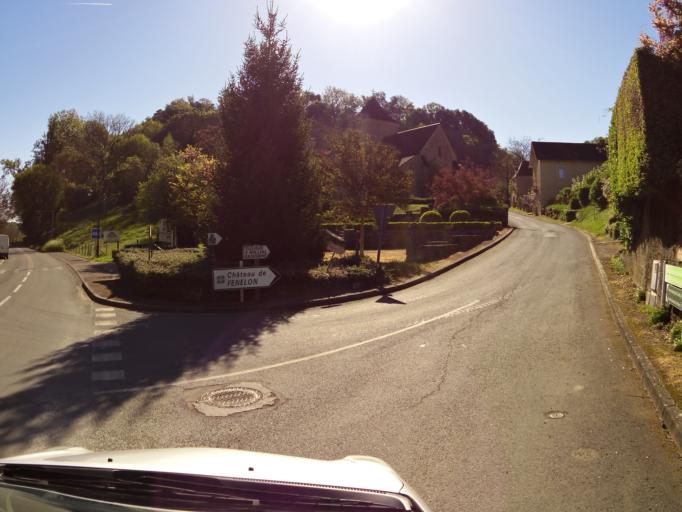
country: FR
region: Aquitaine
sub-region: Departement de la Dordogne
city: Carsac-Aillac
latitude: 44.8453
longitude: 1.3363
